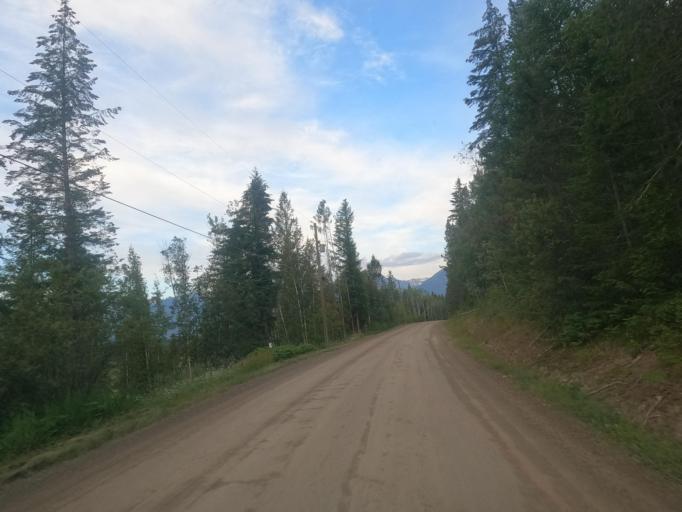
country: CA
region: British Columbia
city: Golden
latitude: 51.4451
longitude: -117.0254
